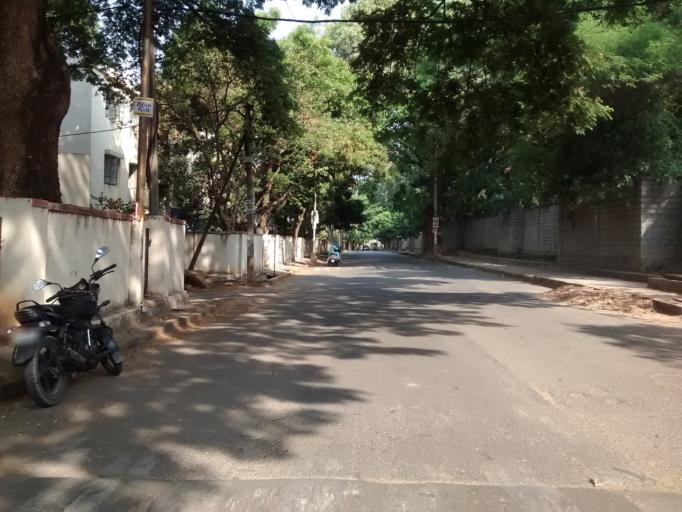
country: IN
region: Karnataka
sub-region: Bangalore Urban
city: Bangalore
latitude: 12.9636
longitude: 77.6659
